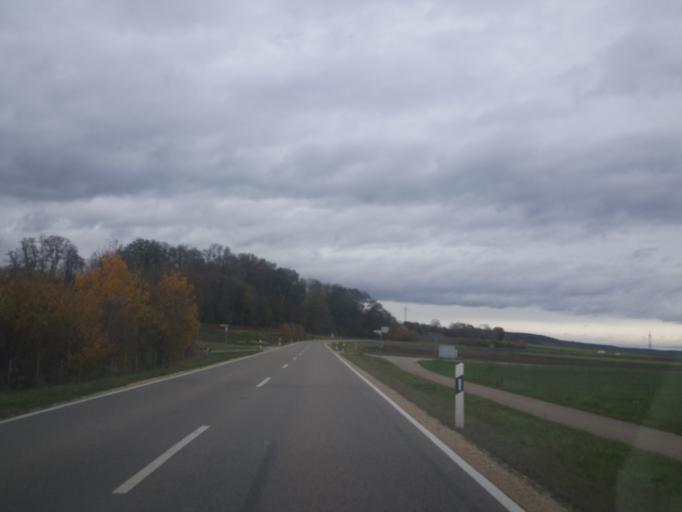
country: DE
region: Bavaria
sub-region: Upper Bavaria
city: Rennertshofen
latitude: 48.7413
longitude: 11.0231
